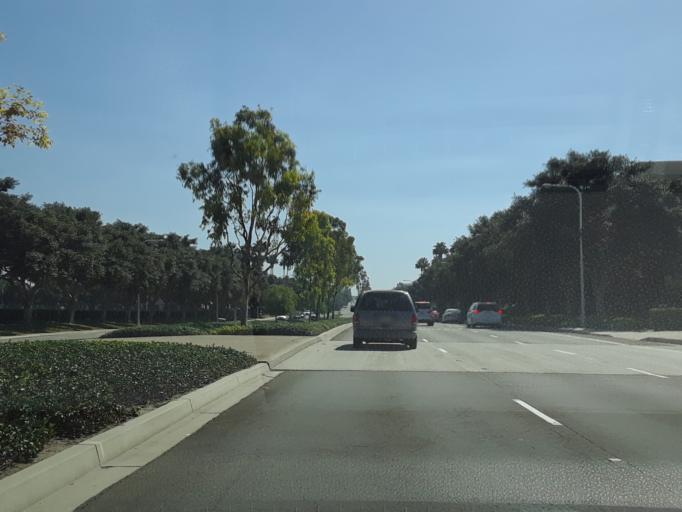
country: US
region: California
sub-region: Orange County
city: Irvine
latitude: 33.6678
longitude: -117.7620
